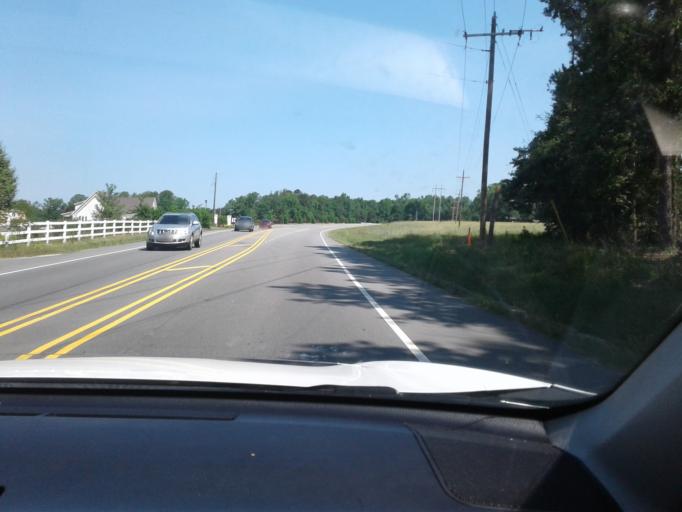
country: US
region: North Carolina
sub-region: Harnett County
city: Lillington
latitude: 35.4335
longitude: -78.8277
